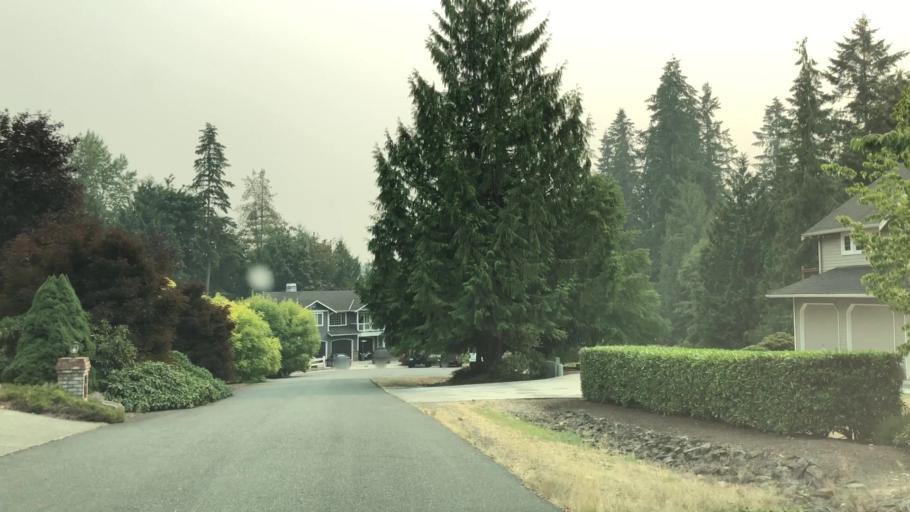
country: US
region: Washington
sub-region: King County
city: Cottage Lake
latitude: 47.7594
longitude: -122.0854
